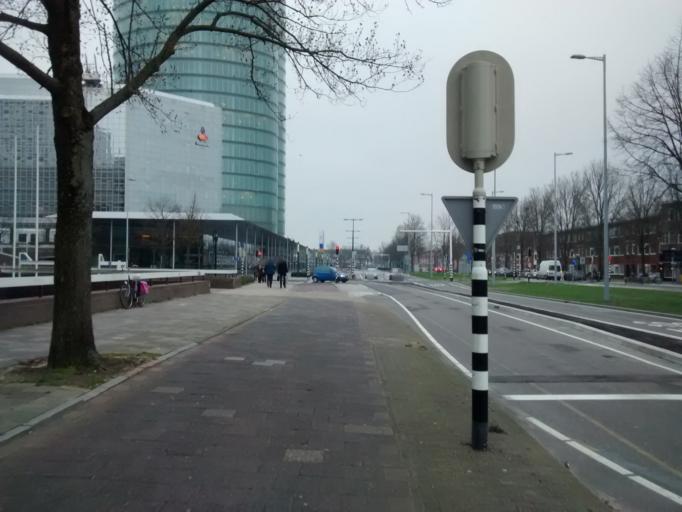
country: NL
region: Utrecht
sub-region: Gemeente Utrecht
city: Utrecht
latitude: 52.0870
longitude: 5.1072
